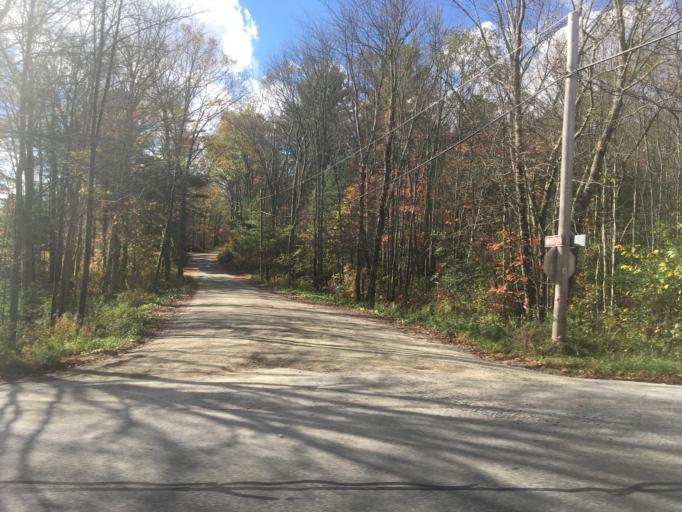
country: US
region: Rhode Island
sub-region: Providence County
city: Foster
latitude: 41.8472
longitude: -71.7043
